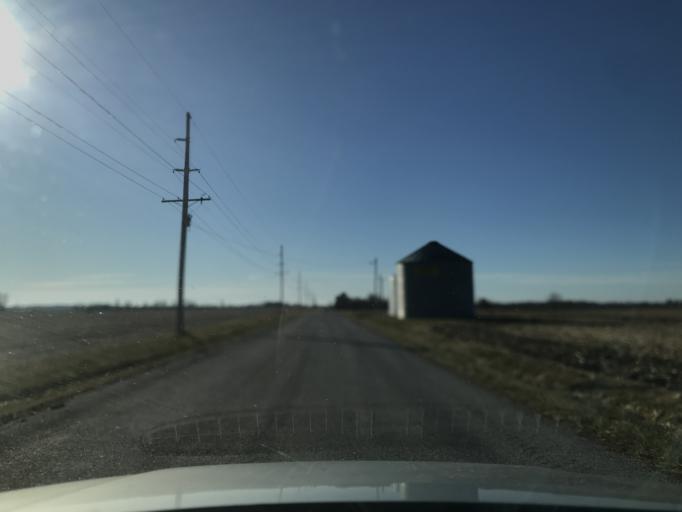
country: US
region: Illinois
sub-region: Hancock County
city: Carthage
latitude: 40.4728
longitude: -91.1782
